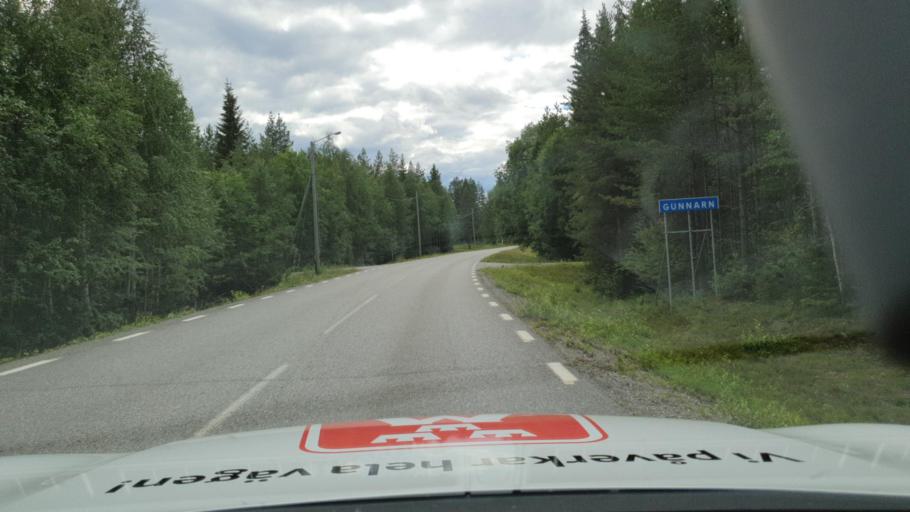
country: SE
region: Vaesterbotten
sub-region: Lycksele Kommun
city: Soderfors
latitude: 65.0156
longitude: 17.7279
